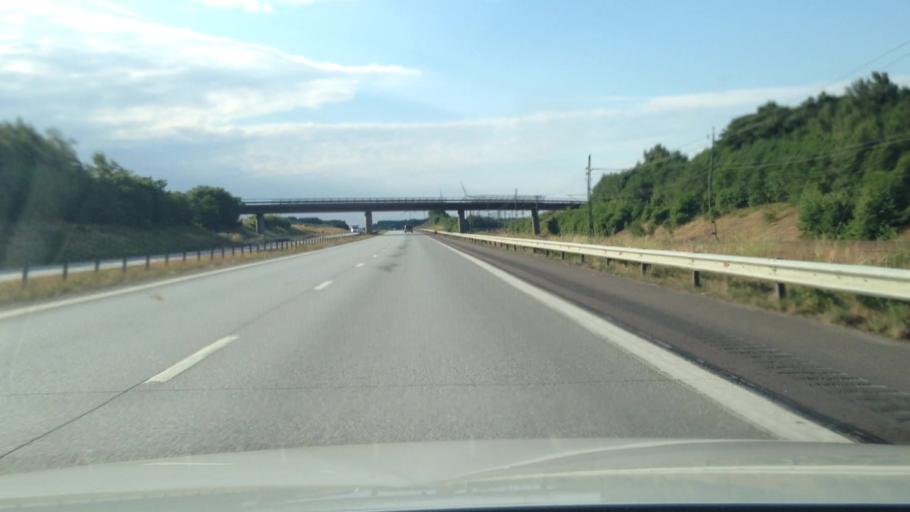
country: SE
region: Halland
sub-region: Falkenbergs Kommun
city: Falkenberg
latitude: 56.9673
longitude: 12.4422
